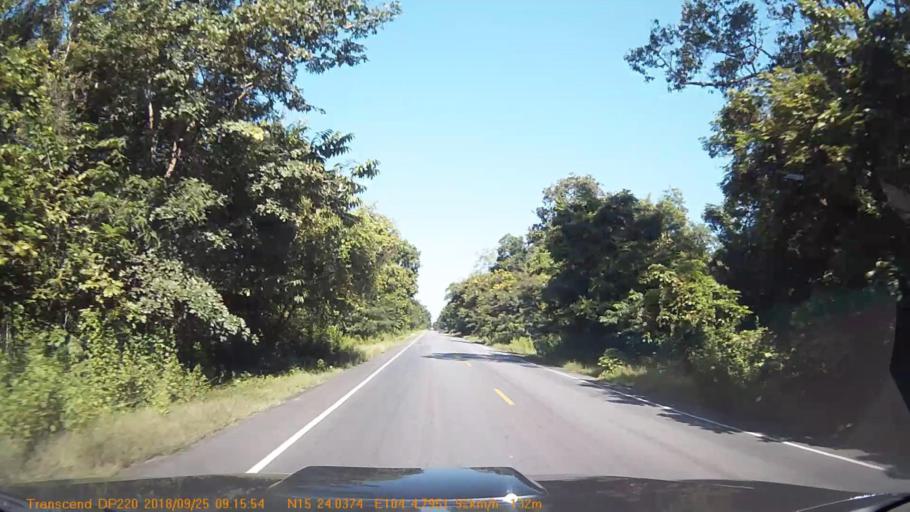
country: TH
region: Sisaket
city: Sila Lat
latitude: 15.4005
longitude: 104.0800
